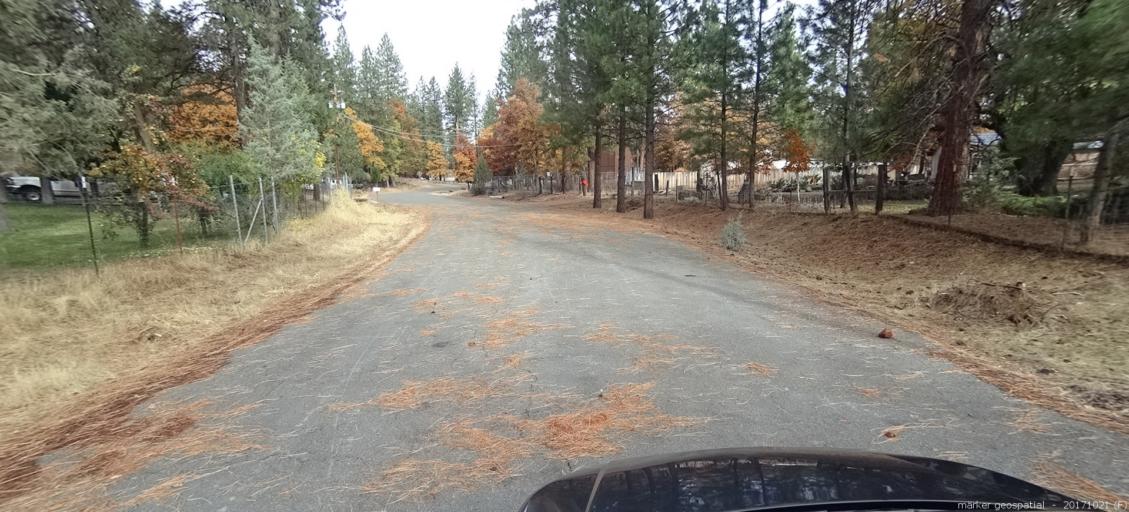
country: US
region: California
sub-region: Shasta County
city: Burney
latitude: 40.9140
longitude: -121.5577
